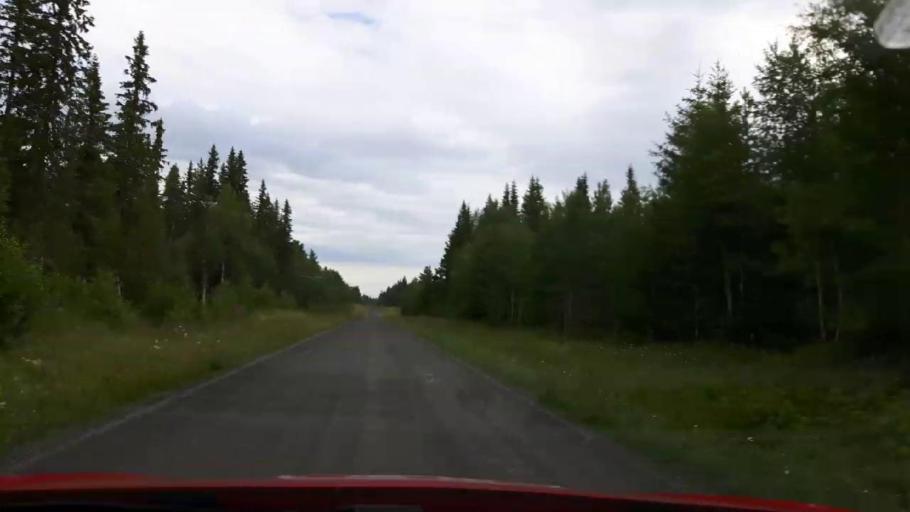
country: SE
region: Jaemtland
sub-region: Stroemsunds Kommun
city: Stroemsund
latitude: 63.5063
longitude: 15.3358
